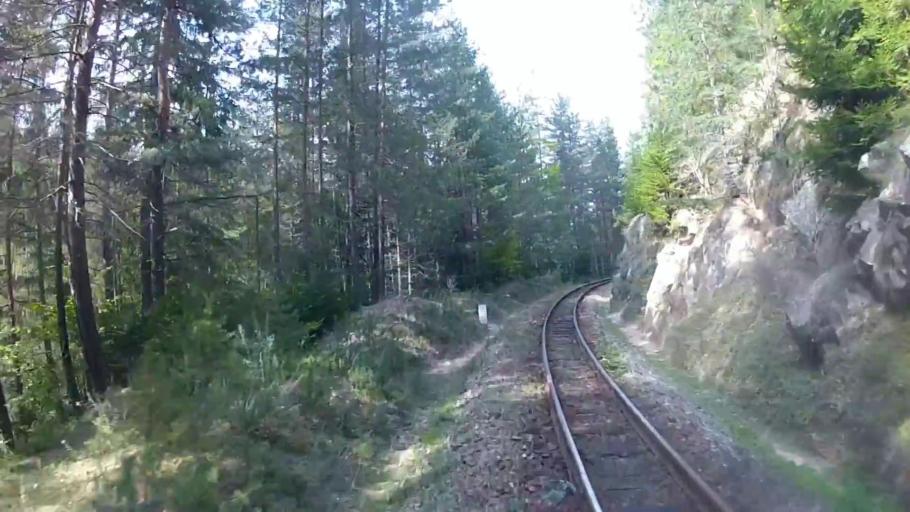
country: BG
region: Blagoevgrad
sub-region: Obshtina Yakoruda
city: Yakoruda
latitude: 42.0362
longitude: 23.7507
